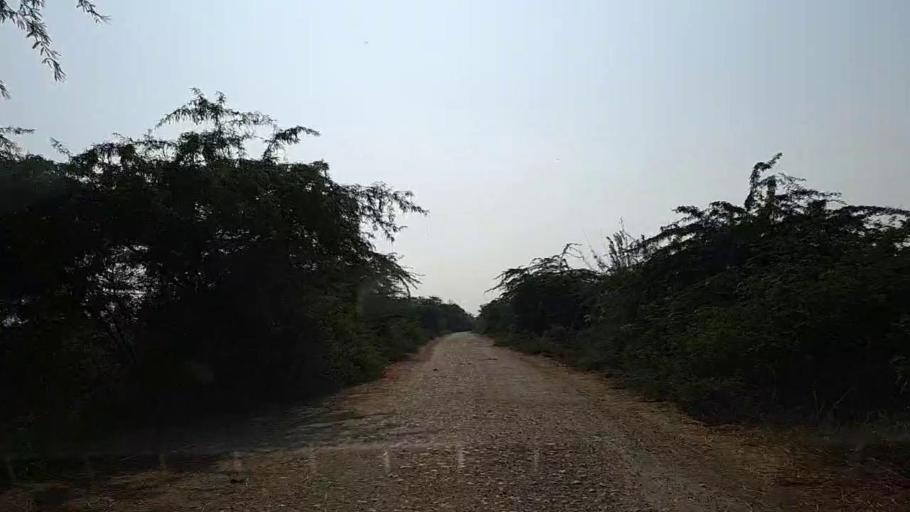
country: PK
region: Sindh
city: Mirpur Sakro
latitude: 24.6304
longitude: 67.6559
